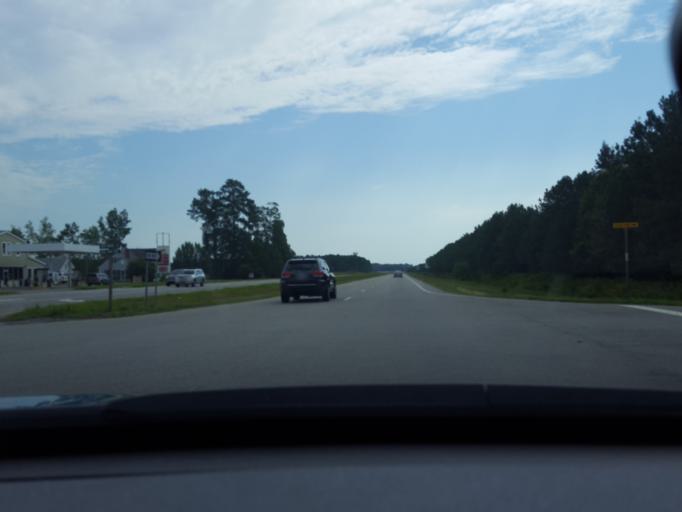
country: US
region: North Carolina
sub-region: Chowan County
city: Edenton
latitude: 36.0380
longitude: -76.7392
